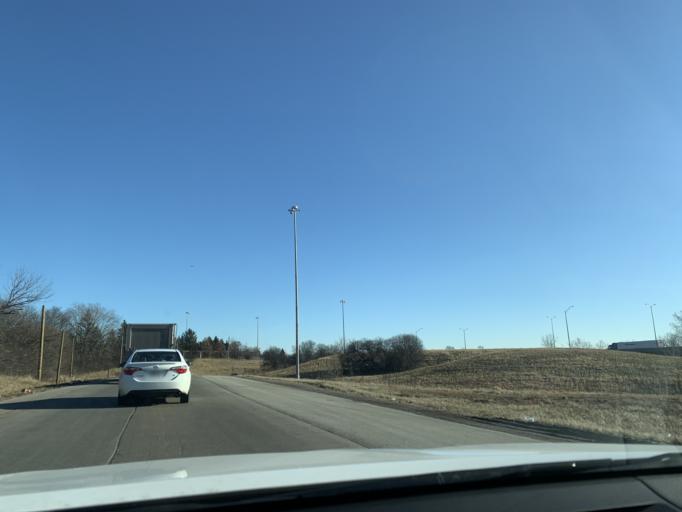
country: US
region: Illinois
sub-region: Cook County
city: Indian Head Park
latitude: 41.7627
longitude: -87.8932
